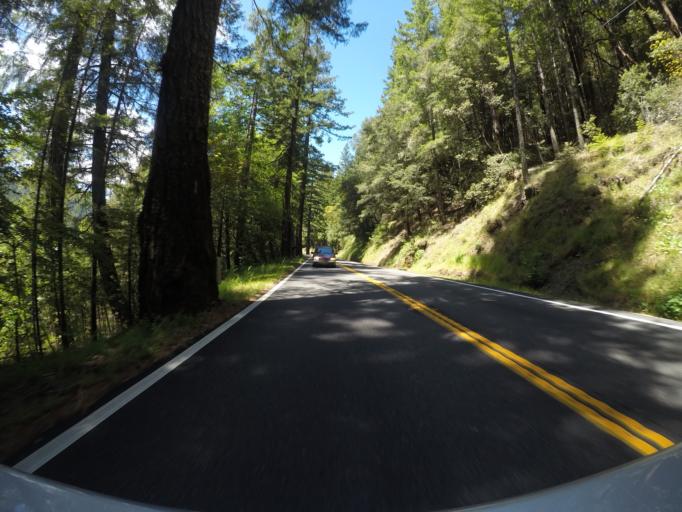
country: US
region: California
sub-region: Humboldt County
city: Redway
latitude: 39.9118
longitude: -123.7575
